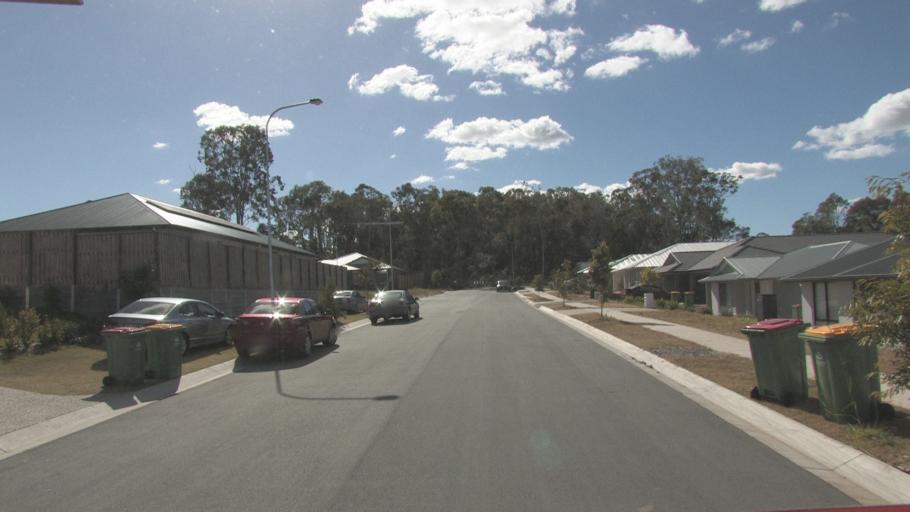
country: AU
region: Queensland
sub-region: Logan
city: Logan Reserve
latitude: -27.7139
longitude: 153.0871
